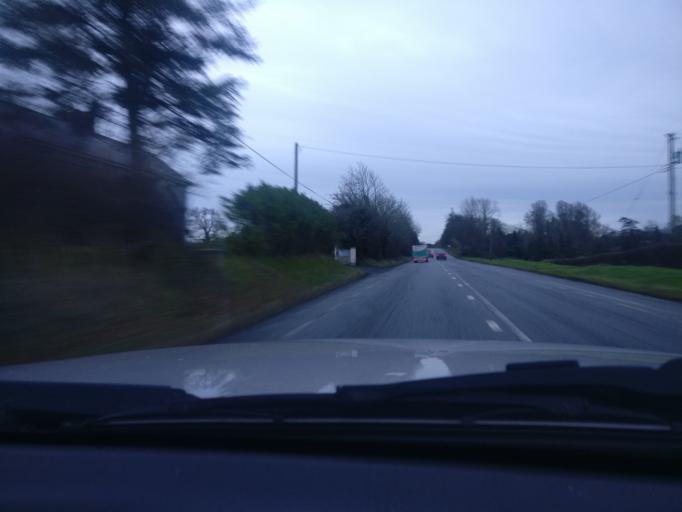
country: IE
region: Leinster
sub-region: An Mhi
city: Kells
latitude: 53.7055
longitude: -6.7971
